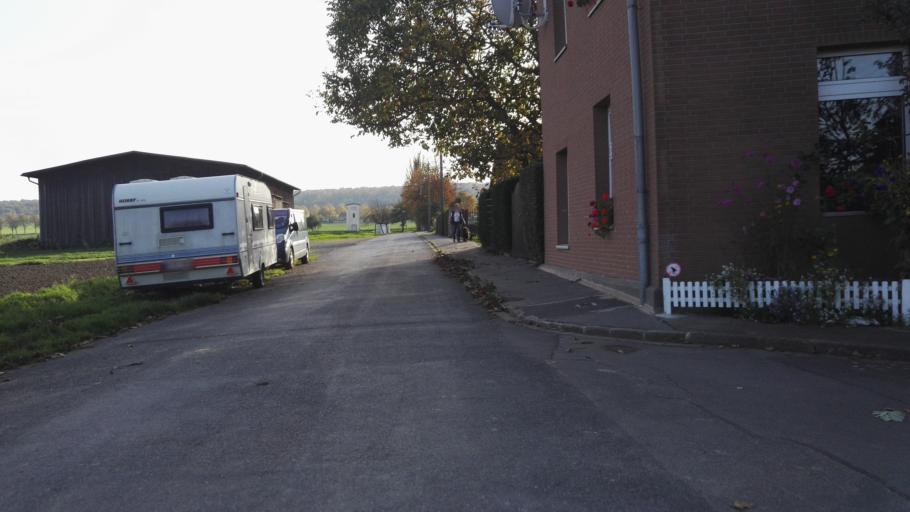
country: DE
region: Lower Saxony
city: Hildesheim
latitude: 52.1492
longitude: 10.0114
